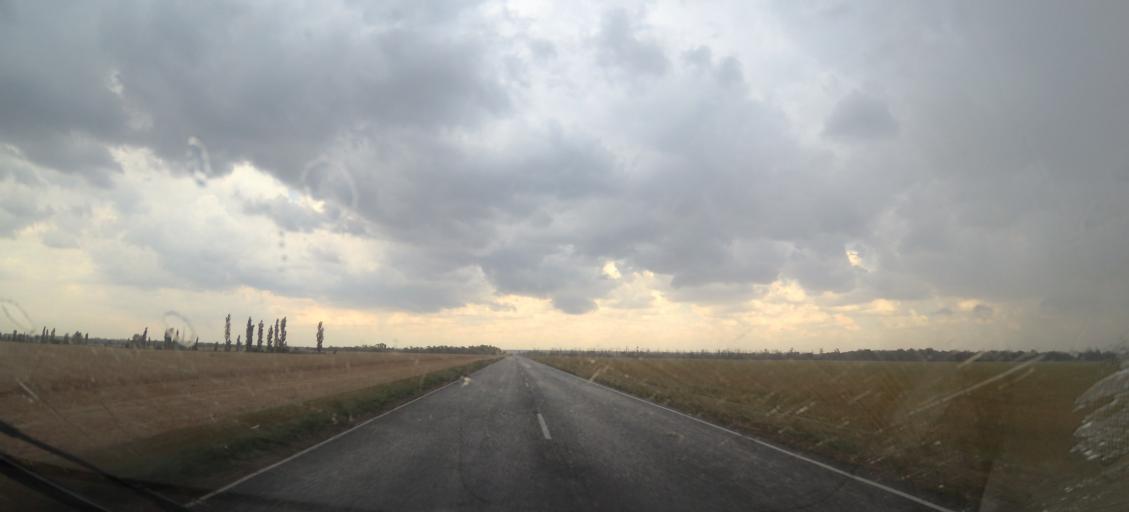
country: RU
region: Rostov
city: Orlovskiy
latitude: 46.8688
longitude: 41.9738
